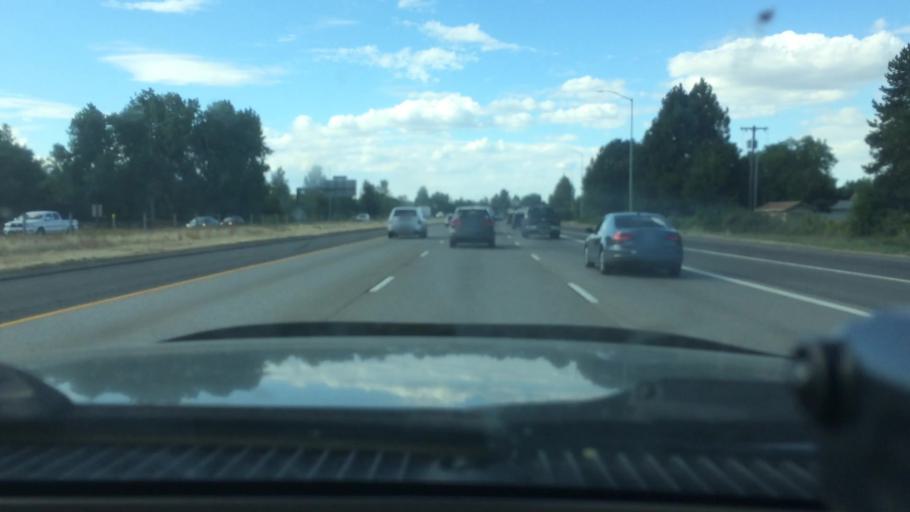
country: US
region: Oregon
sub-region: Marion County
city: Four Corners
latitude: 44.9188
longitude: -122.9898
